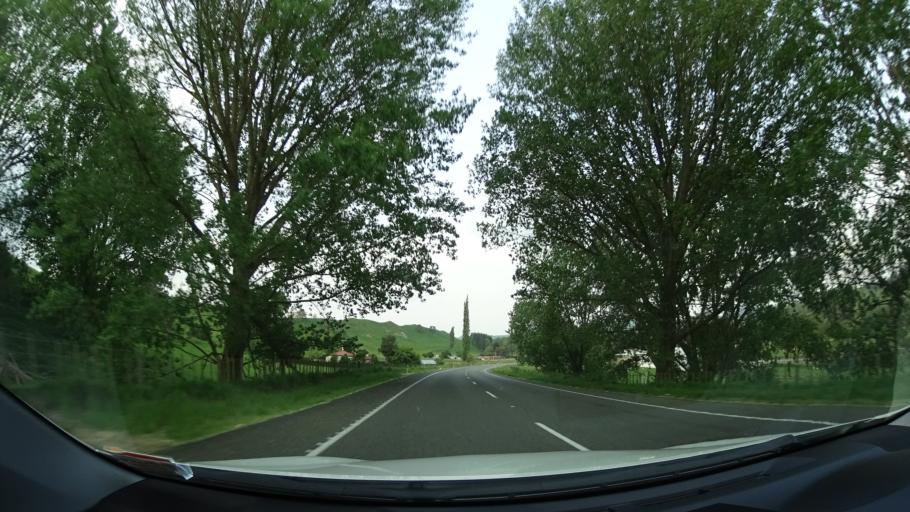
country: NZ
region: Manawatu-Wanganui
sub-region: Ruapehu District
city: Waiouru
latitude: -39.7381
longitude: 175.8404
